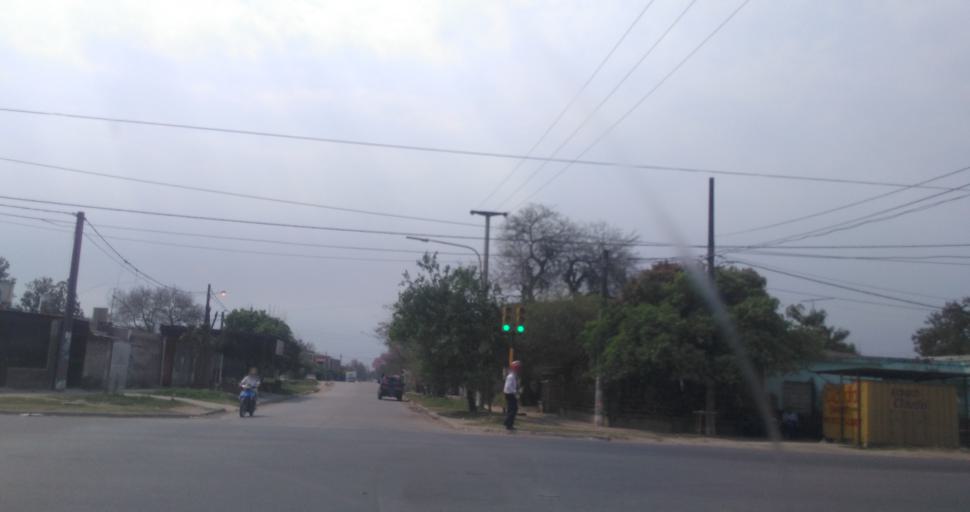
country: AR
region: Chaco
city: Fontana
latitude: -27.4249
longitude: -59.0307
